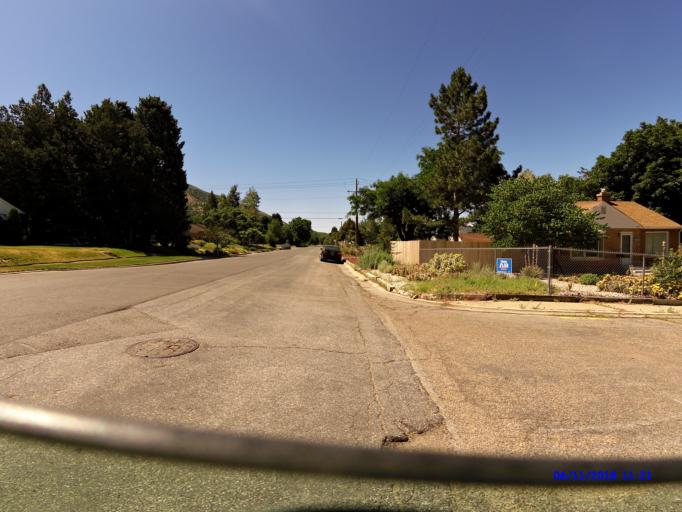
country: US
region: Utah
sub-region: Weber County
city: Ogden
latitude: 41.2233
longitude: -111.9344
